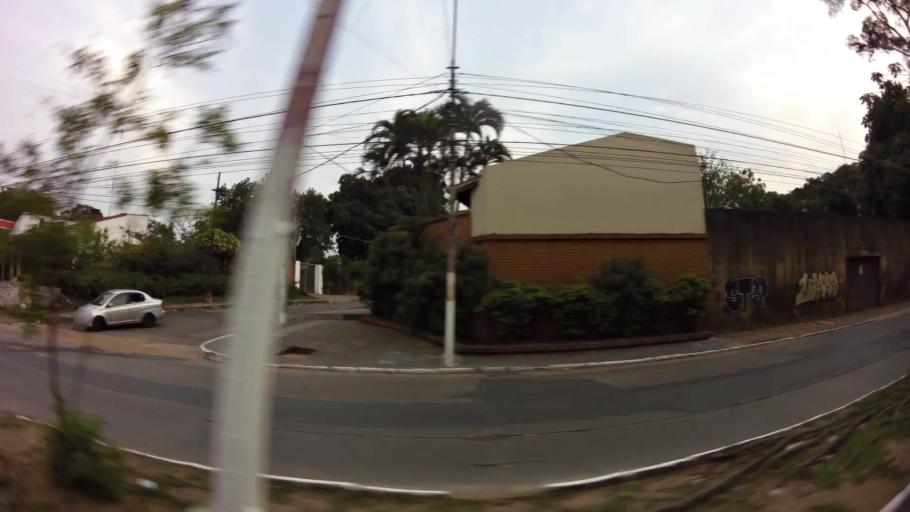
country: PY
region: Central
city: Lambare
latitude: -25.3424
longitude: -57.6323
